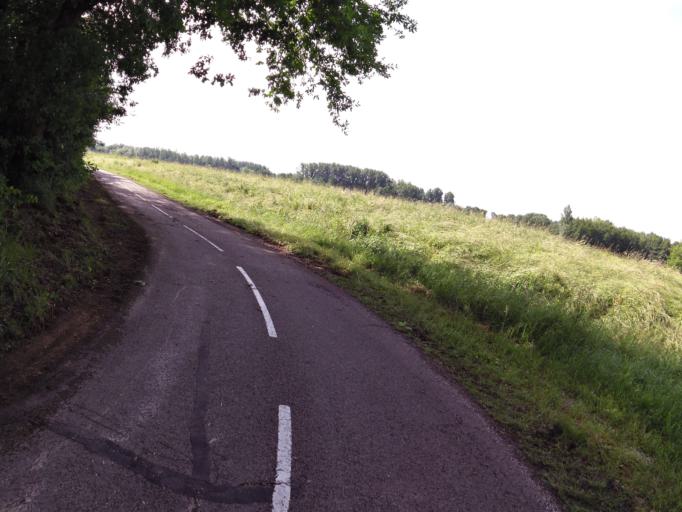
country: FR
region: Champagne-Ardenne
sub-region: Departement de l'Aube
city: Verrieres
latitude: 48.2648
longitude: 4.1788
